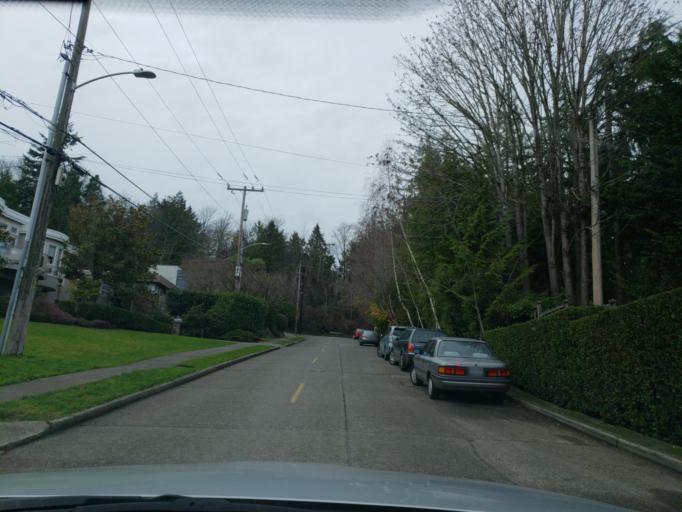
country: US
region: Washington
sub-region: King County
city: Seattle
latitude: 47.6661
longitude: -122.4080
